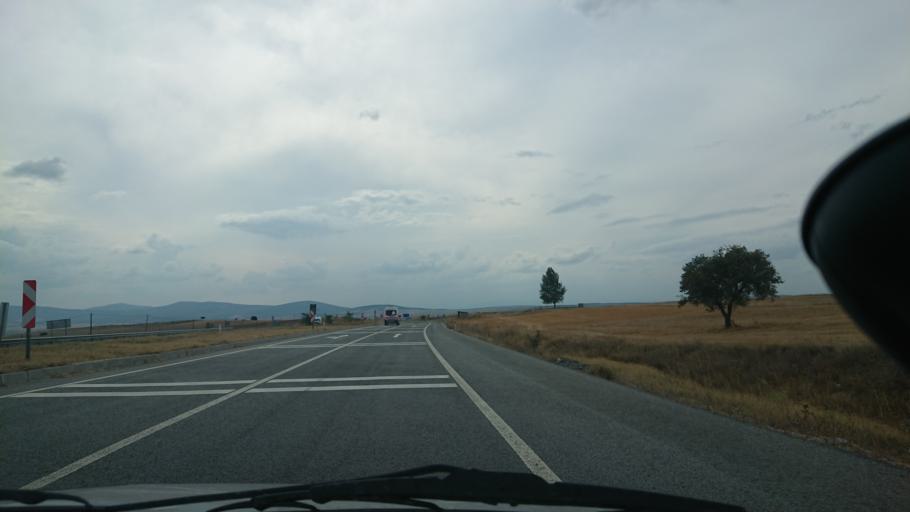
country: TR
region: Kuetahya
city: Aslanapa
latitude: 39.2609
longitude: 29.8818
